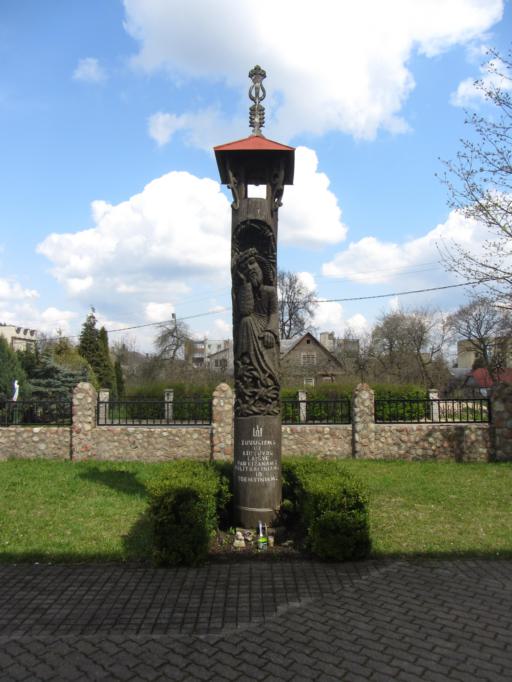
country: LT
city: Lentvaris
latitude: 54.6418
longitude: 25.0483
